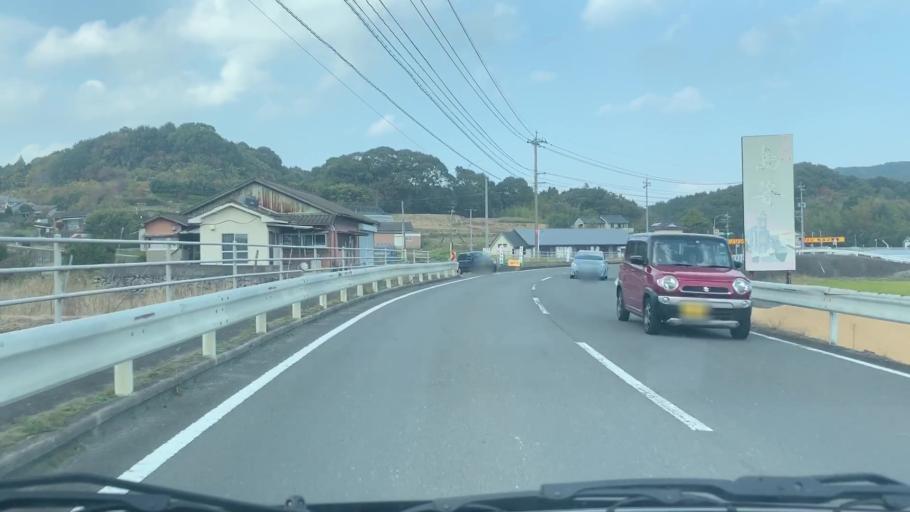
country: JP
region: Nagasaki
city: Togitsu
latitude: 32.9679
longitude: 129.7809
